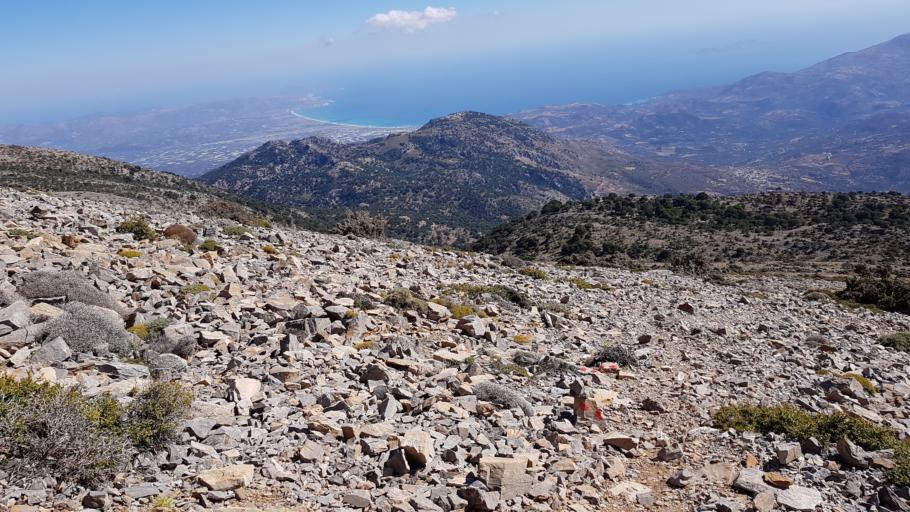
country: GR
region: Crete
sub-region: Nomos Rethymnis
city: Zoniana
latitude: 35.2088
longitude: 24.7678
